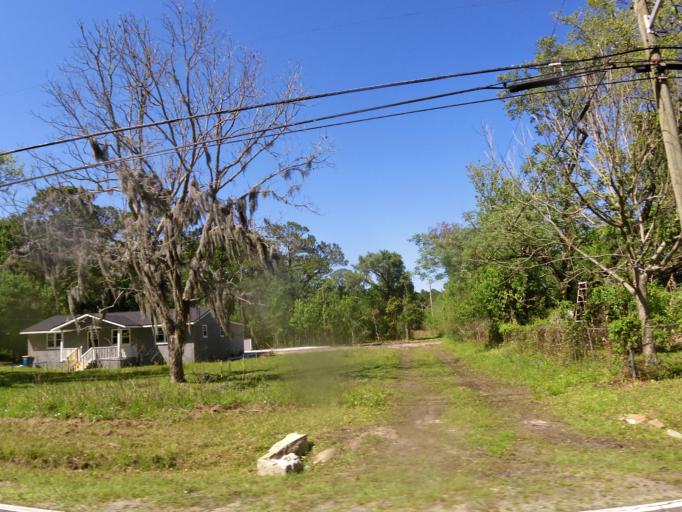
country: US
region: Florida
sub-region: Duval County
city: Jacksonville
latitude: 30.4509
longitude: -81.6096
